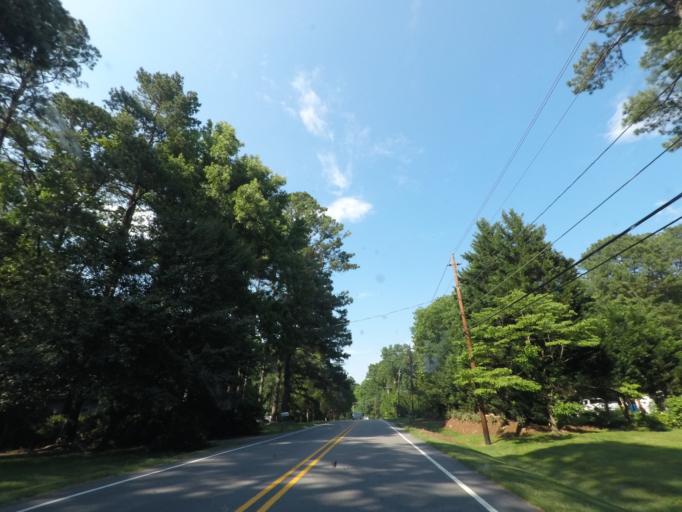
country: US
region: North Carolina
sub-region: Durham County
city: Durham
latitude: 35.9482
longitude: -78.9404
